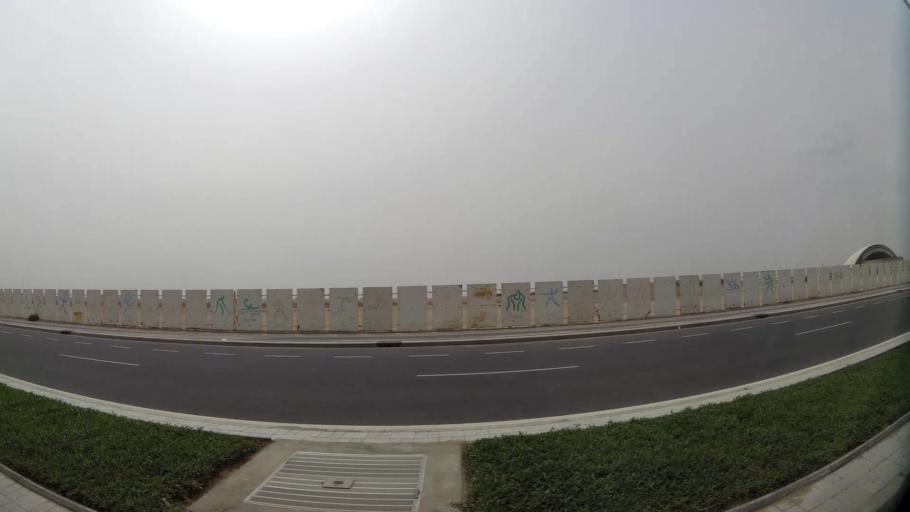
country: QA
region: Baladiyat ad Dawhah
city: Doha
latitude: 25.2267
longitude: 51.5359
